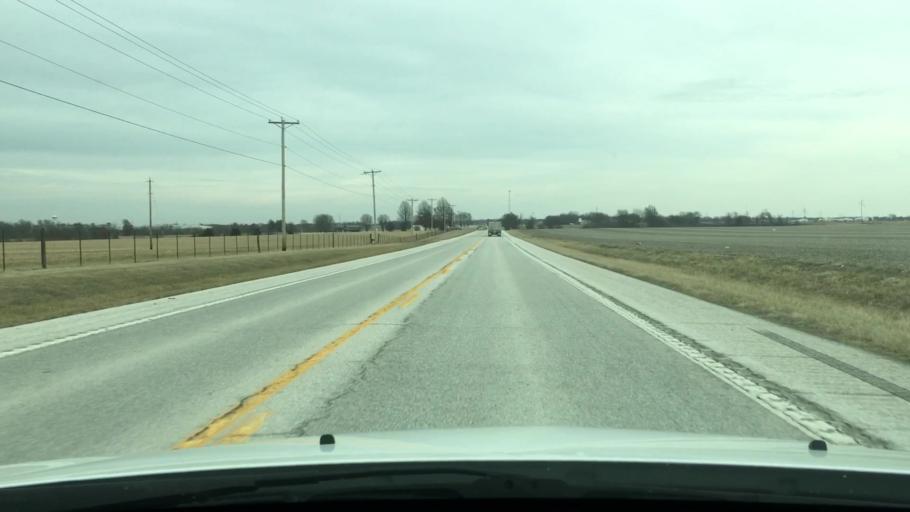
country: US
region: Missouri
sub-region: Pike County
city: Bowling Green
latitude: 39.3443
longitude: -91.2526
